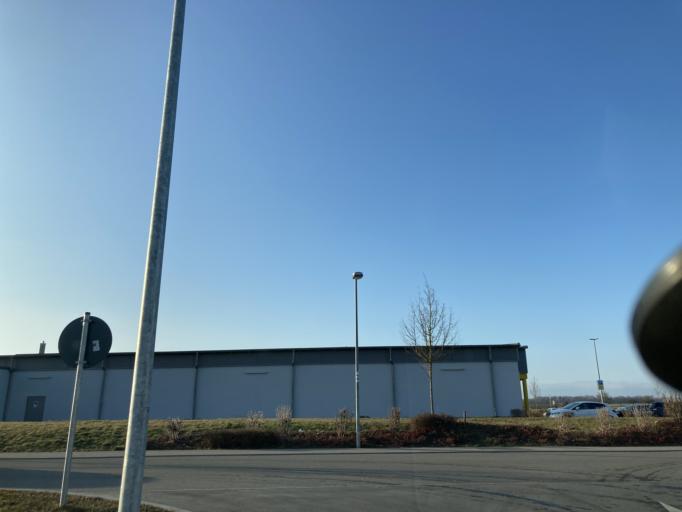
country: DE
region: Baden-Wuerttemberg
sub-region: Tuebingen Region
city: Hirrlingen
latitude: 48.4146
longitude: 8.8966
